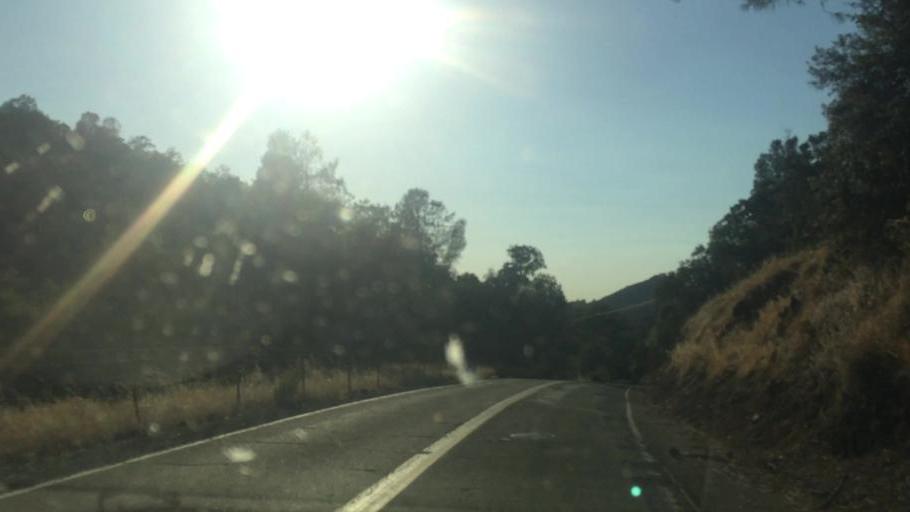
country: US
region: California
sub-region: Amador County
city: Plymouth
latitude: 38.4807
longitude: -120.8692
